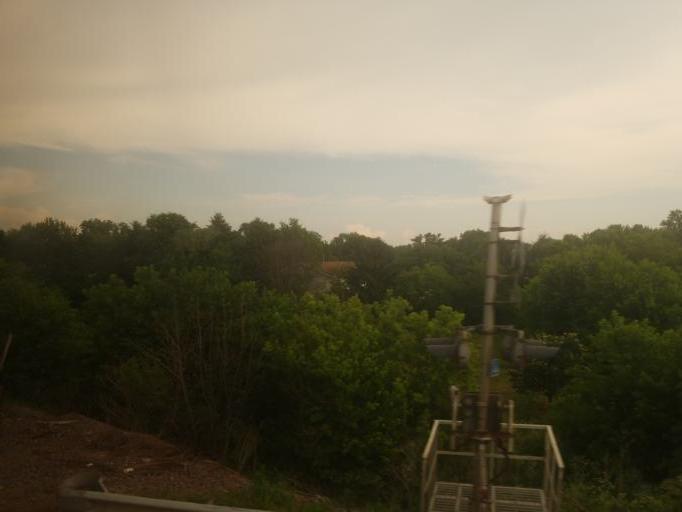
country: US
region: Illinois
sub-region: Bureau County
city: Princeton
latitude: 41.3861
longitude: -89.4743
